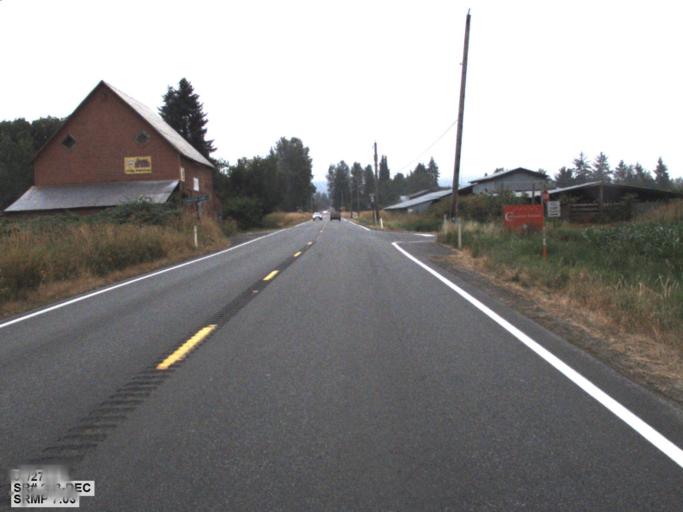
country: US
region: Washington
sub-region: King County
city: Carnation
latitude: 47.6628
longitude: -121.9092
